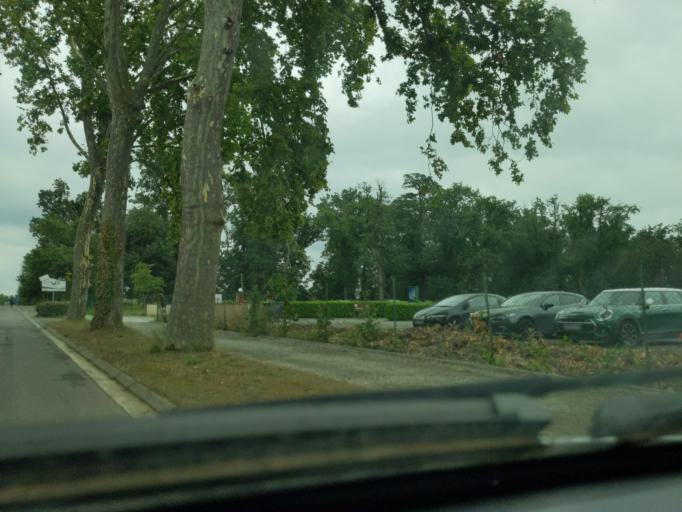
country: FR
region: Midi-Pyrenees
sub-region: Departement de la Haute-Garonne
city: Cugnaux
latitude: 43.5759
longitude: 1.3643
